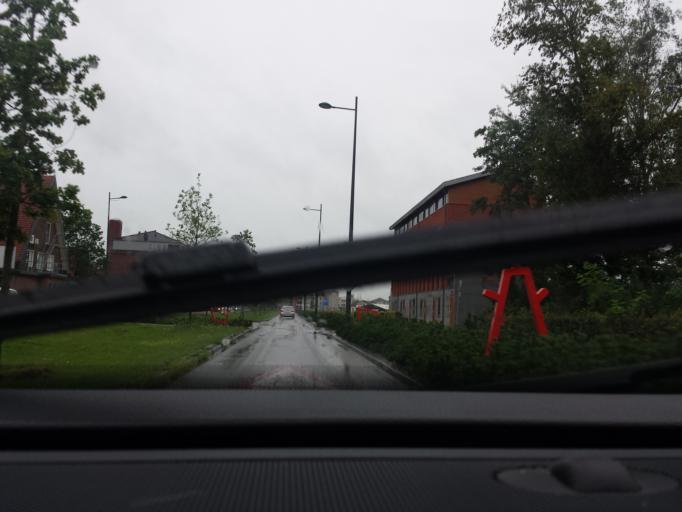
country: NL
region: Gelderland
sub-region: Gemeente Doetinchem
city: Doetinchem
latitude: 51.9710
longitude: 6.2874
